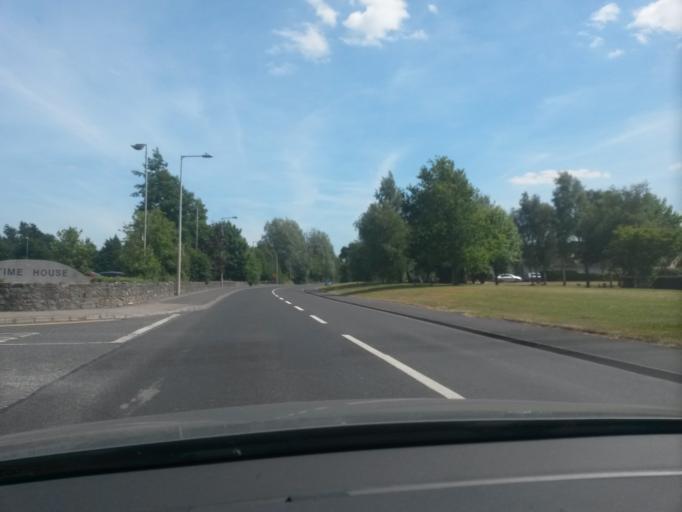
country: IE
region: Leinster
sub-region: Kildare
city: Naas
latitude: 53.2162
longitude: -6.6532
